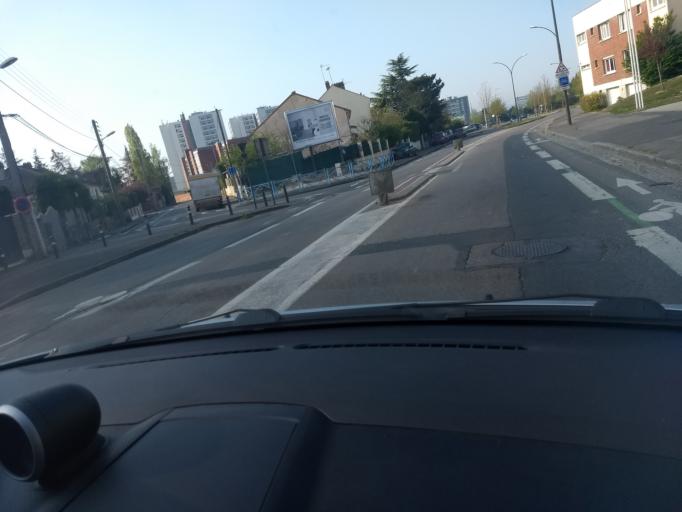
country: FR
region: Picardie
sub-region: Departement de la Somme
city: Rivery
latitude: 49.9132
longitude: 2.3179
